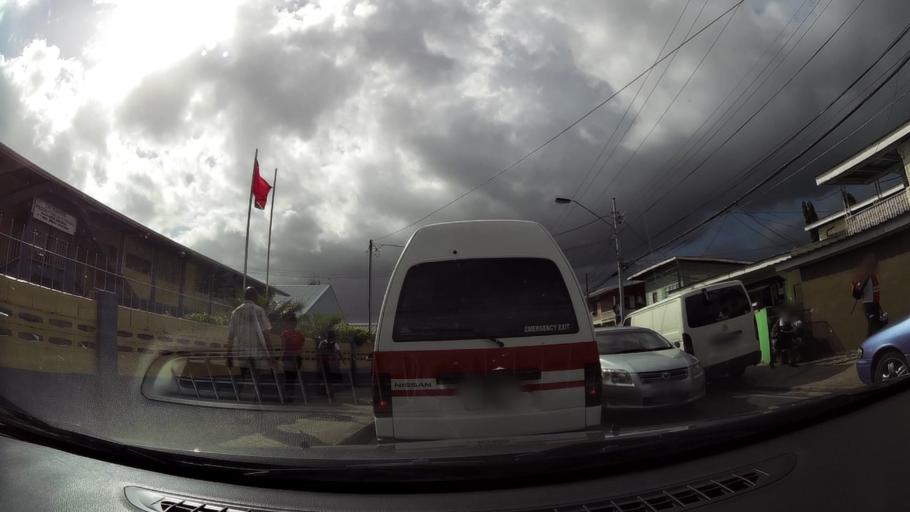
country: TT
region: Tunapuna/Piarco
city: Paradise
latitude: 10.6439
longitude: -61.3620
